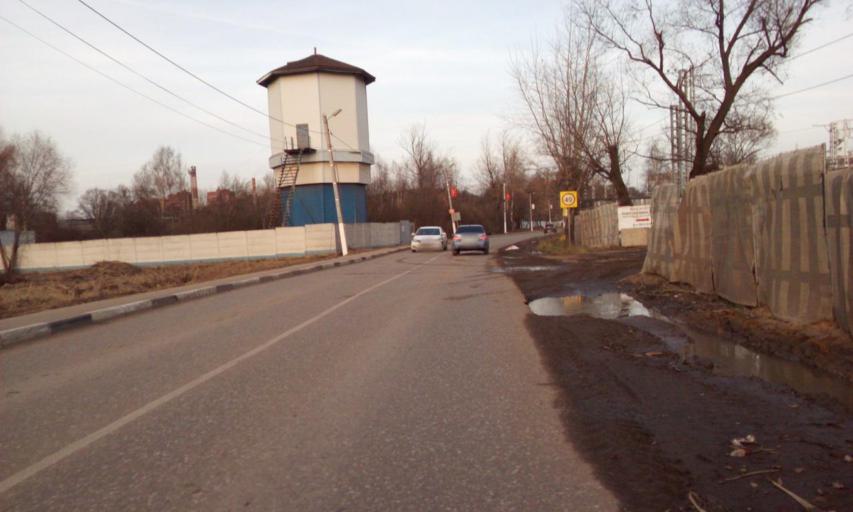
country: RU
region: Moskovskaya
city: Aprelevka
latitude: 55.5496
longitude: 37.0644
